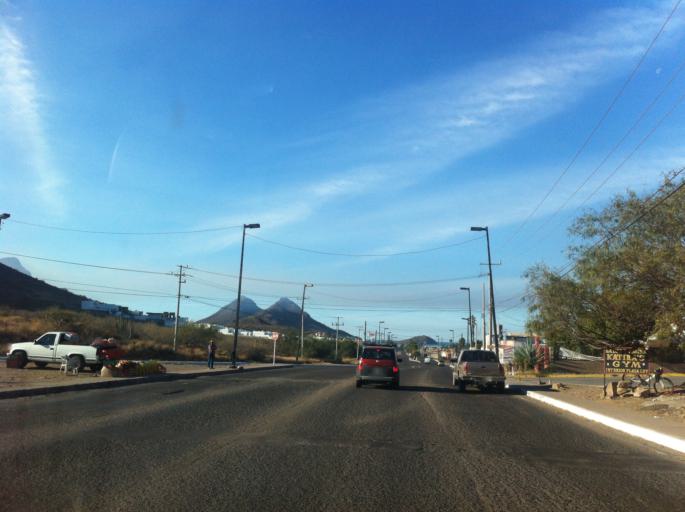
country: MX
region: Sonora
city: Heroica Guaymas
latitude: 27.9286
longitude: -110.9281
